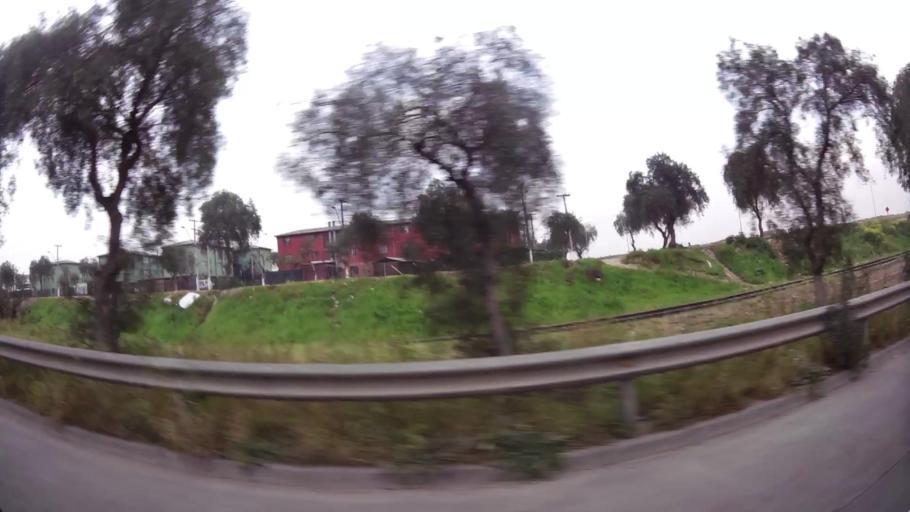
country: CL
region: Santiago Metropolitan
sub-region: Provincia de Santiago
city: Lo Prado
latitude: -33.4894
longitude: -70.7202
